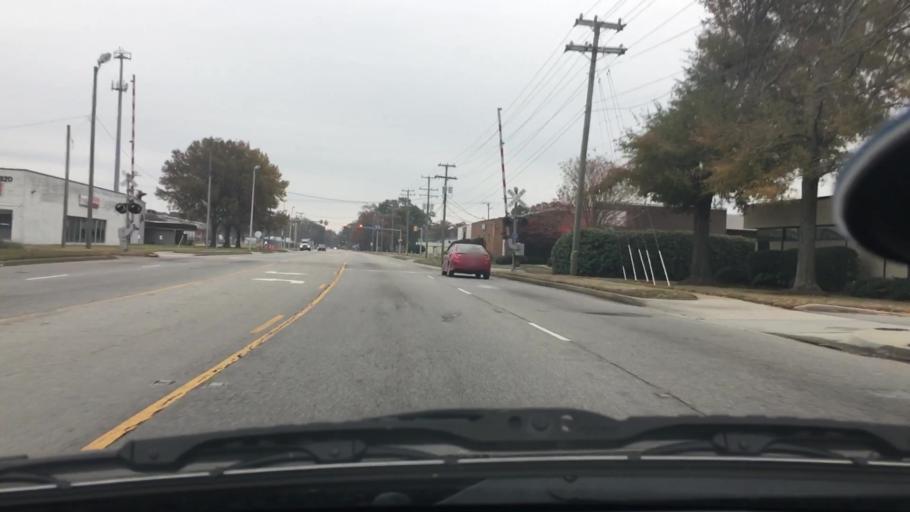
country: US
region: Virginia
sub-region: City of Norfolk
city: Norfolk
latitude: 36.8603
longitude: -76.2432
